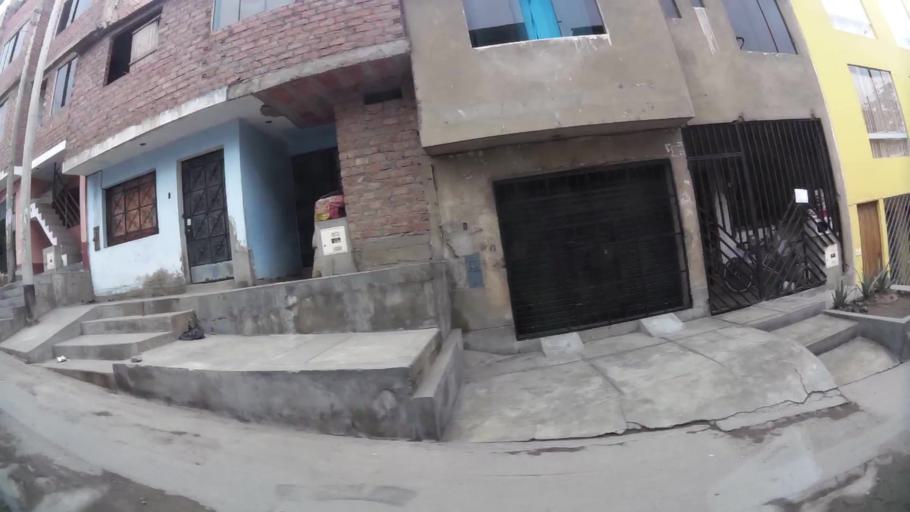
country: PE
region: Lima
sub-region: Lima
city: Surco
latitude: -12.1674
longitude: -76.9606
